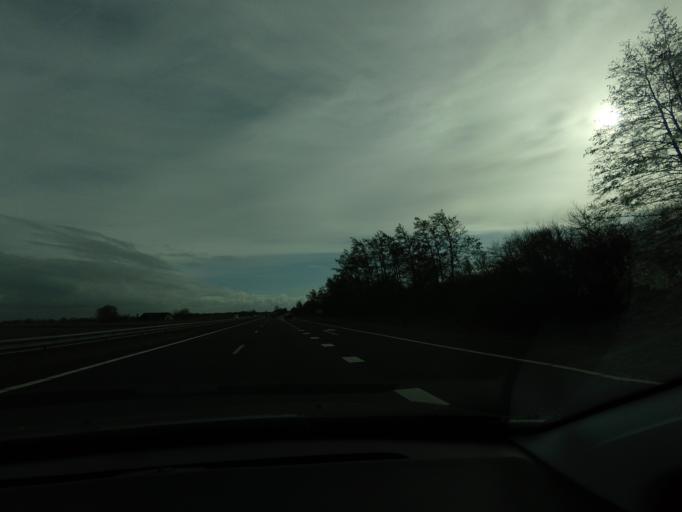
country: NL
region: Friesland
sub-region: Gemeente Boarnsterhim
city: Reduzum
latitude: 53.1180
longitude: 5.8098
